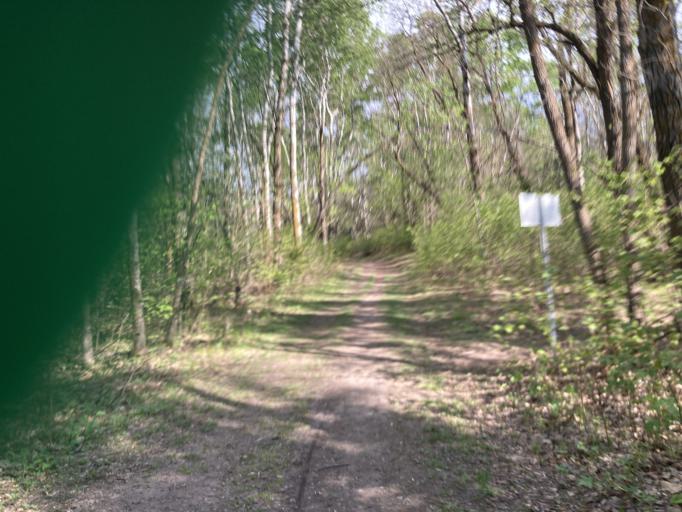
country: CA
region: Manitoba
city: Brandon
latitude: 49.7182
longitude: -99.9054
